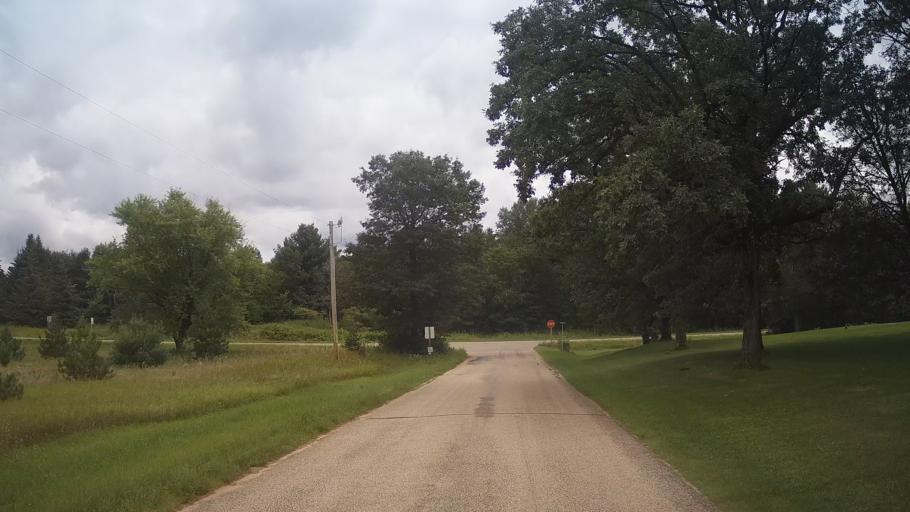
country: US
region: Wisconsin
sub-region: Adams County
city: Friendship
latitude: 44.0325
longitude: -89.8893
